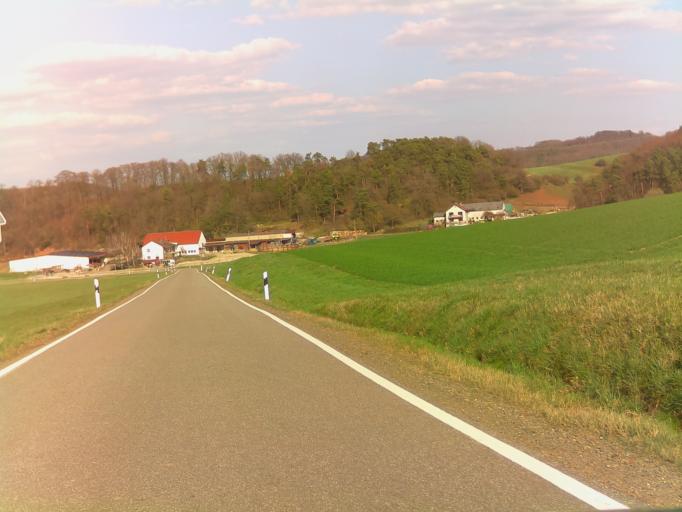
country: DE
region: Rheinland-Pfalz
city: Limbach
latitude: 49.7341
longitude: 7.5388
